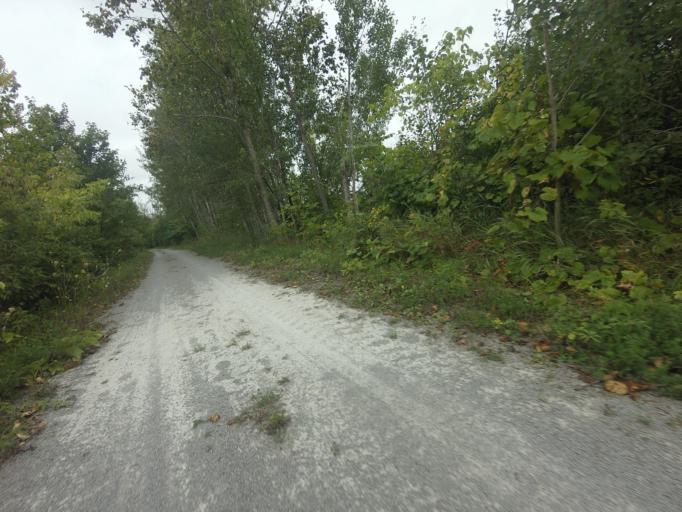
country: CA
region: Ontario
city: Uxbridge
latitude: 44.2997
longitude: -78.9250
